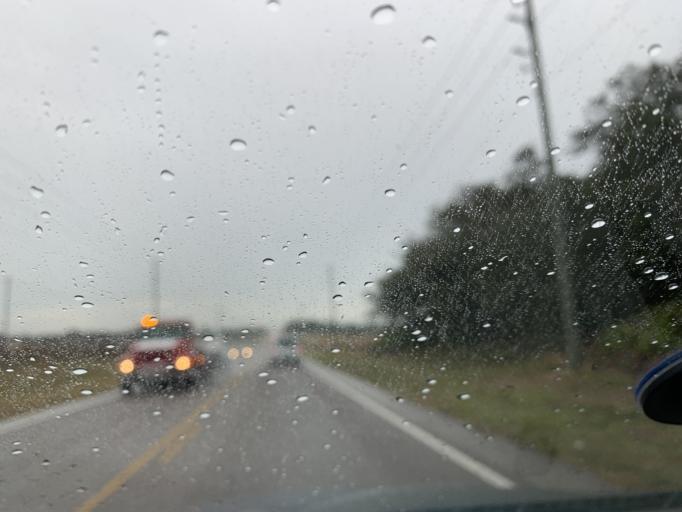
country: US
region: Florida
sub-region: Pasco County
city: Shady Hills
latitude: 28.4338
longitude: -82.5192
